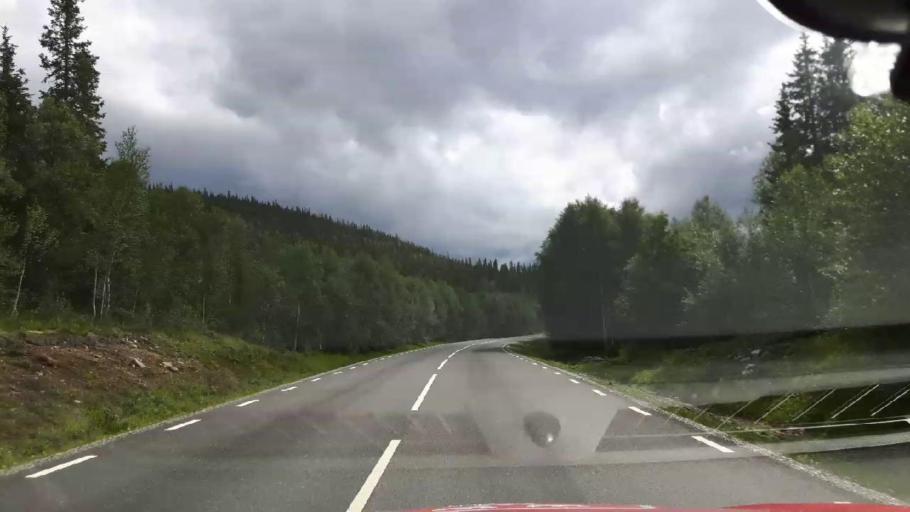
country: NO
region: Nord-Trondelag
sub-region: Royrvik
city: Royrvik
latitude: 64.8864
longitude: 14.1990
